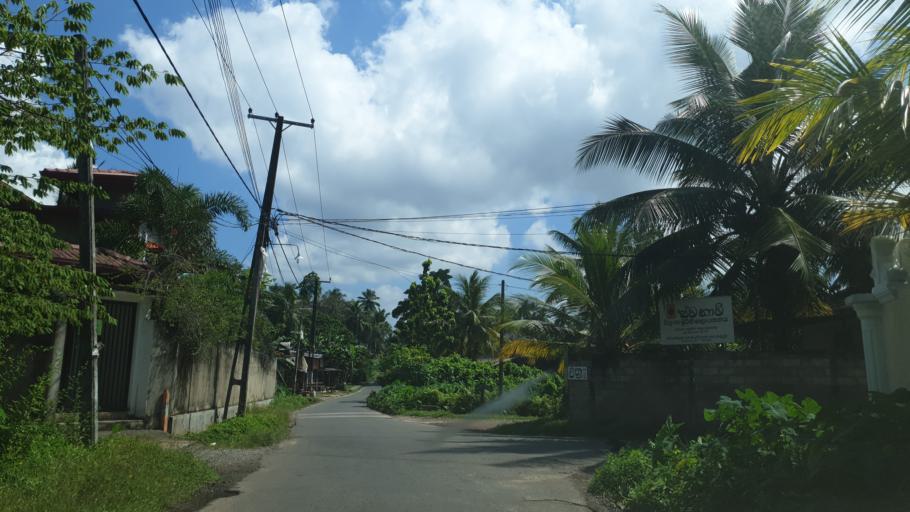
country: LK
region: Western
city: Panadura
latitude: 6.6740
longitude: 79.9331
